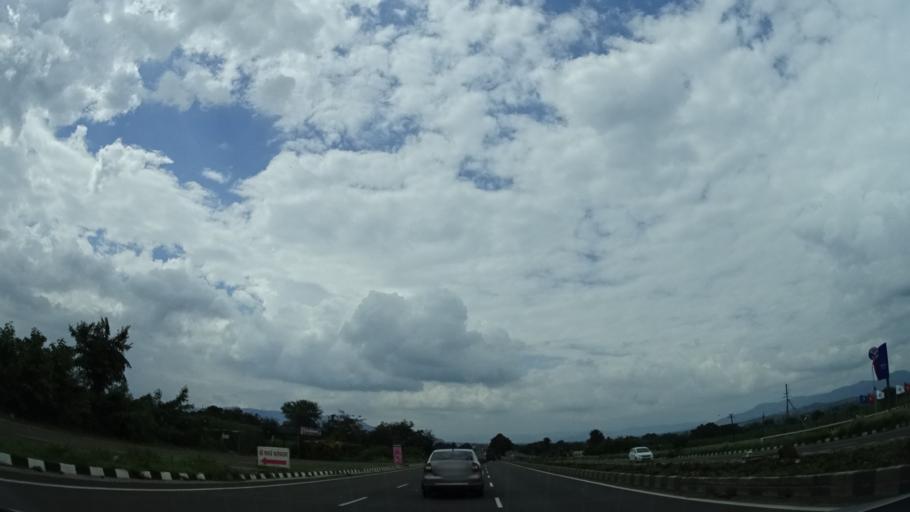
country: IN
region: Maharashtra
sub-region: Satara Division
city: Satara
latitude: 17.7980
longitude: 73.9770
